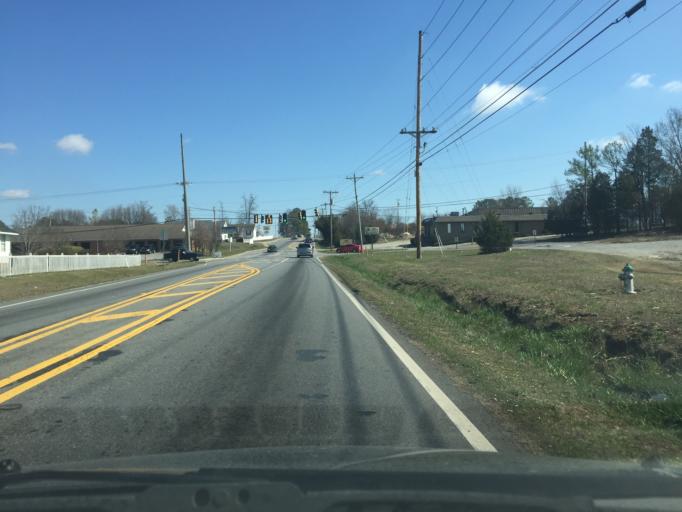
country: US
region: Georgia
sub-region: Catoosa County
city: Fort Oglethorpe
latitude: 34.9570
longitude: -85.2387
